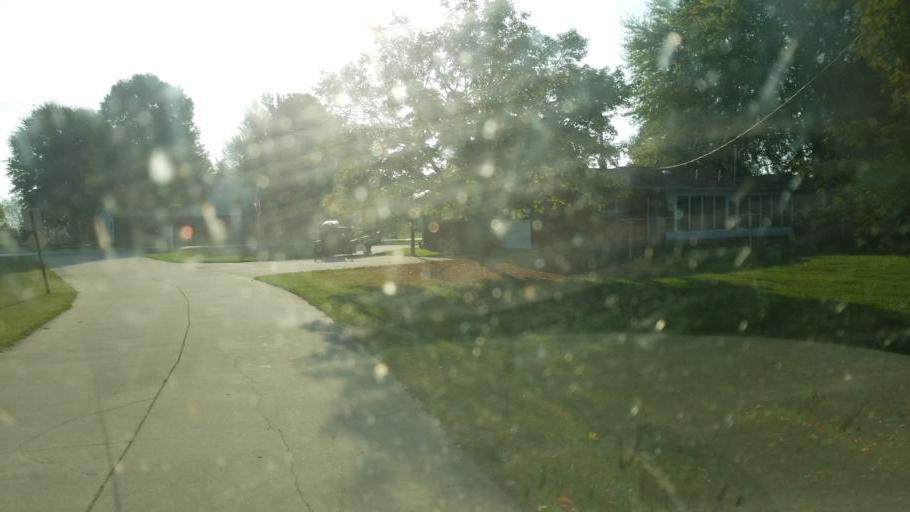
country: US
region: Indiana
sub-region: LaGrange County
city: Topeka
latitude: 41.6723
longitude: -85.5570
